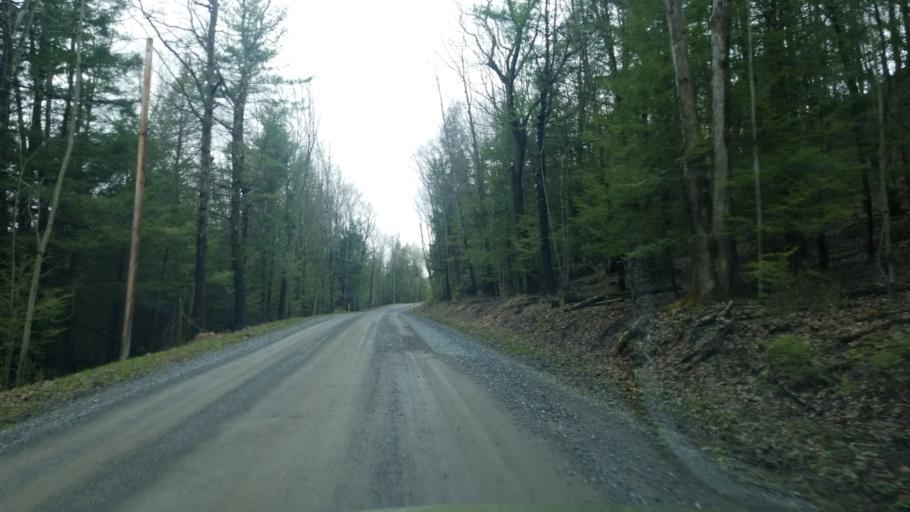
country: US
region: Pennsylvania
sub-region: Clearfield County
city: Shiloh
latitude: 41.1176
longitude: -78.3413
